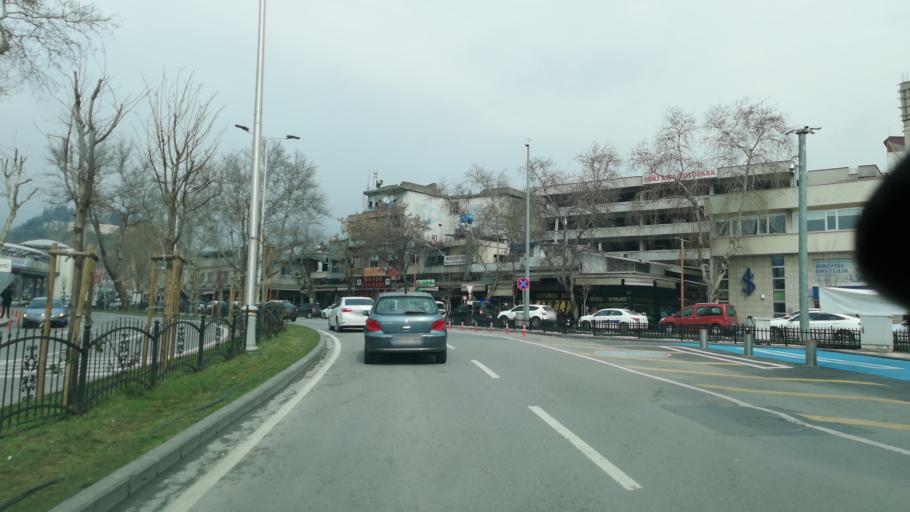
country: TR
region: Kahramanmaras
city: Kahramanmaras
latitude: 37.5810
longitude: 36.9273
